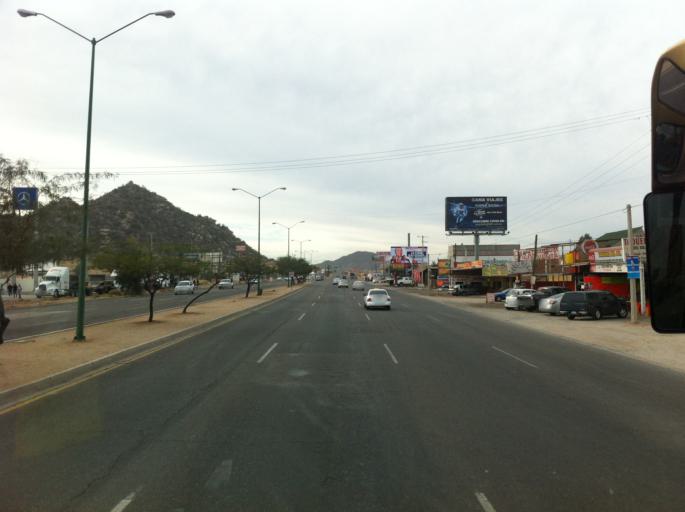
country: MX
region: Sonora
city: Hermosillo
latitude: 29.0284
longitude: -110.9601
